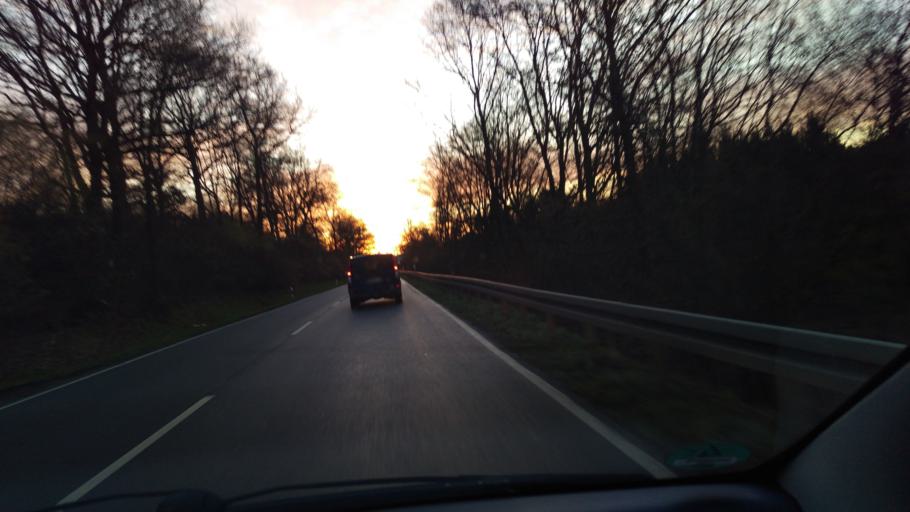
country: DE
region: Hesse
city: Kirtorf
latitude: 50.7709
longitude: 9.0959
